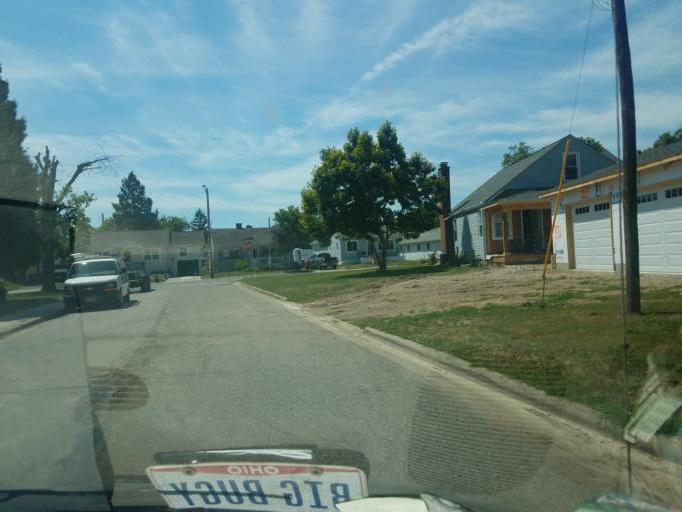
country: US
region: Ohio
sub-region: Franklin County
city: Grove City
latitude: 39.8777
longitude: -83.0953
